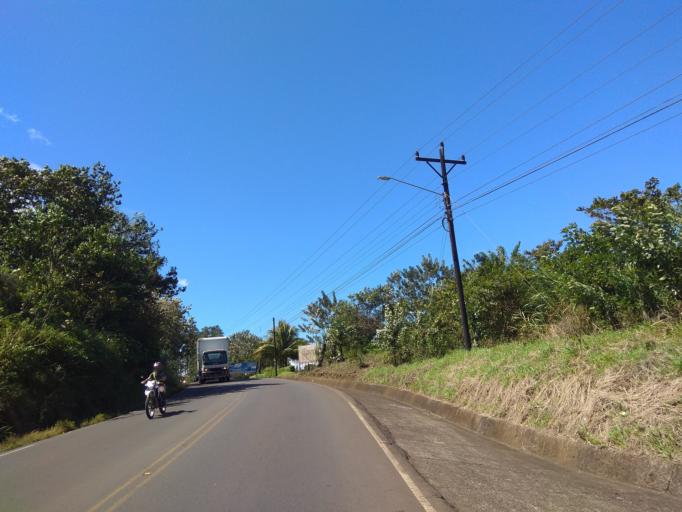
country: CR
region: Alajuela
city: Quesada
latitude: 10.3612
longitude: -84.4518
